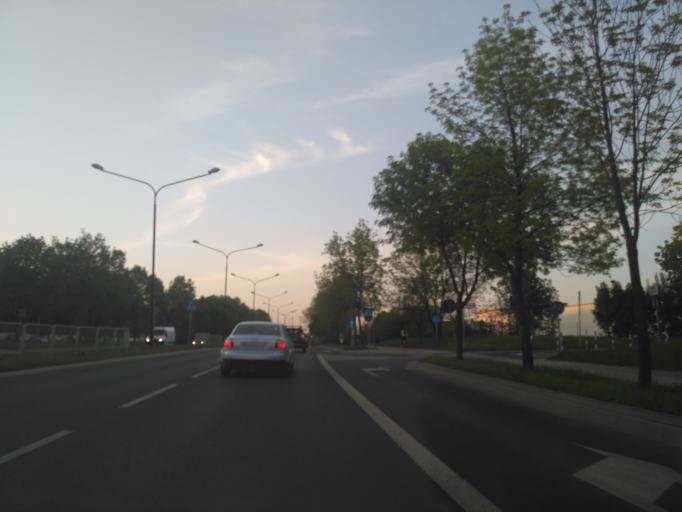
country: PL
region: Lublin Voivodeship
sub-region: Powiat lubelski
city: Lublin
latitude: 51.2648
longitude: 22.5584
